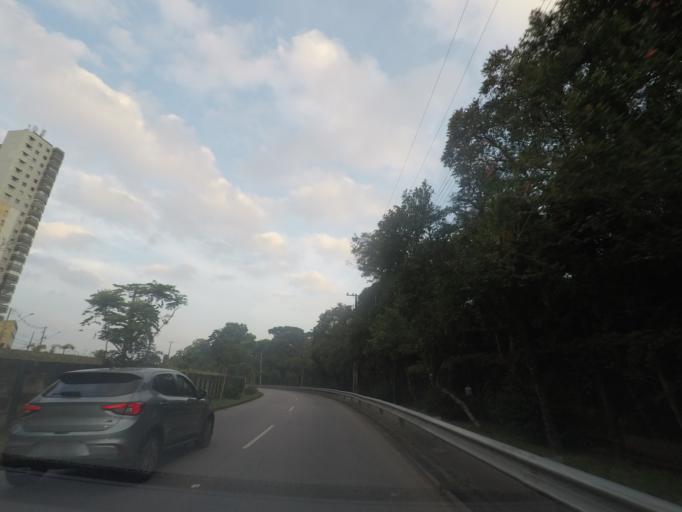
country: BR
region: Parana
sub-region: Curitiba
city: Curitiba
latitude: -25.4413
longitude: -49.2366
